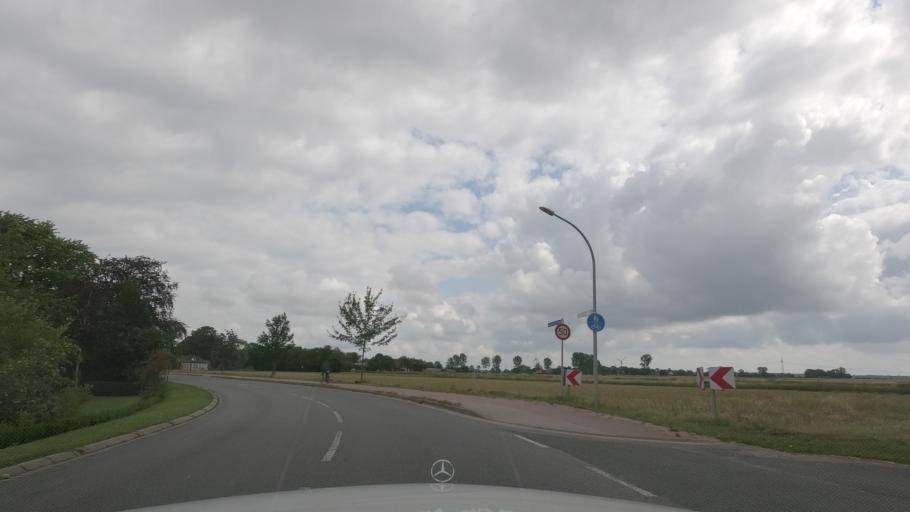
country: DE
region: Lower Saxony
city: Neuenkirchen
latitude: 53.2814
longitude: 8.5320
